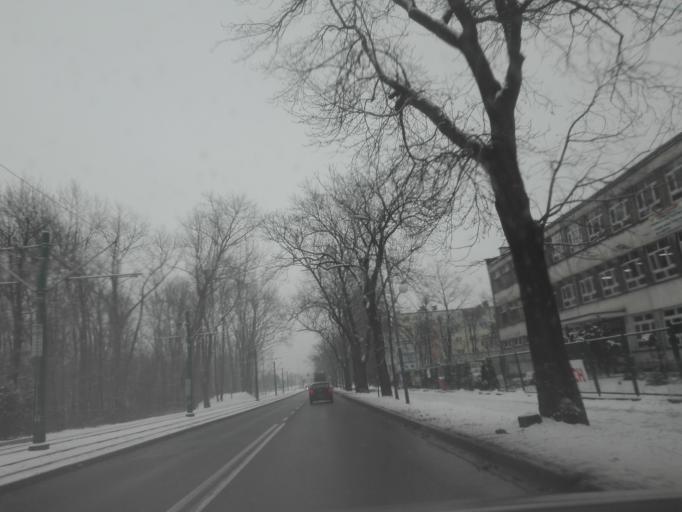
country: PL
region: Silesian Voivodeship
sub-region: Chorzow
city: Chorzow
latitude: 50.2710
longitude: 18.9711
